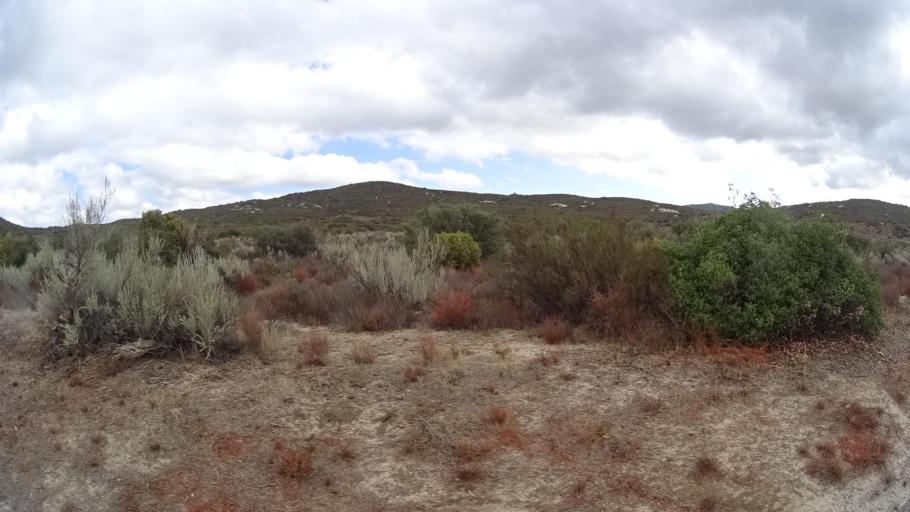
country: US
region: California
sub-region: San Diego County
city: Campo
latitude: 32.6654
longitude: -116.4289
